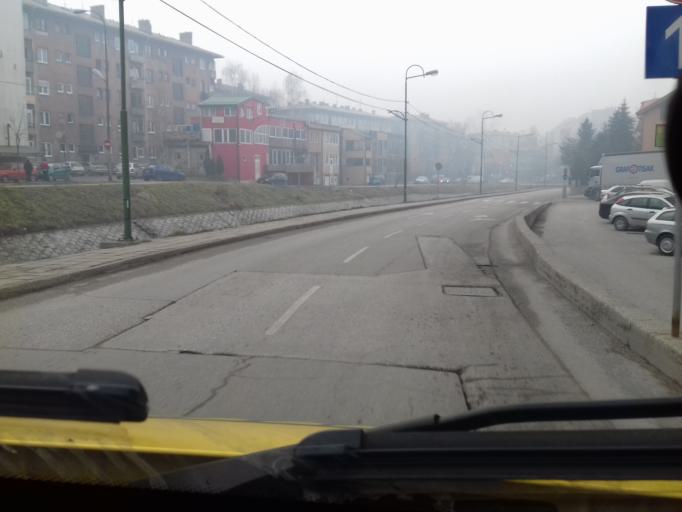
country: BA
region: Federation of Bosnia and Herzegovina
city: Kakanj
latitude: 44.1267
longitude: 18.1155
